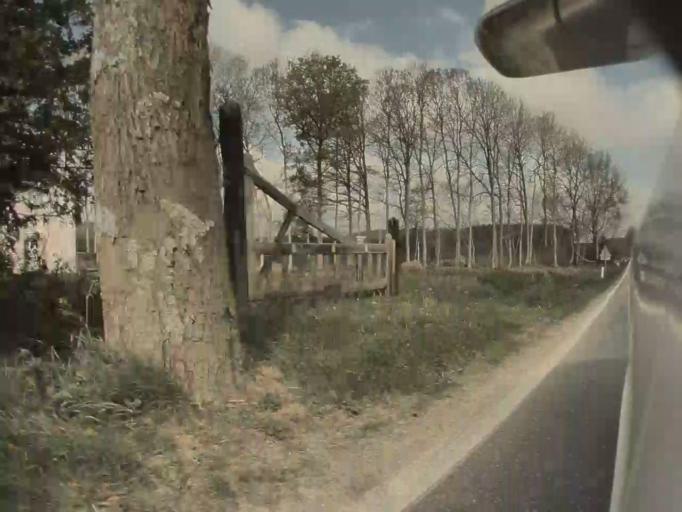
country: BE
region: Wallonia
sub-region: Province du Luxembourg
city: Tellin
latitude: 50.0591
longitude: 5.2077
